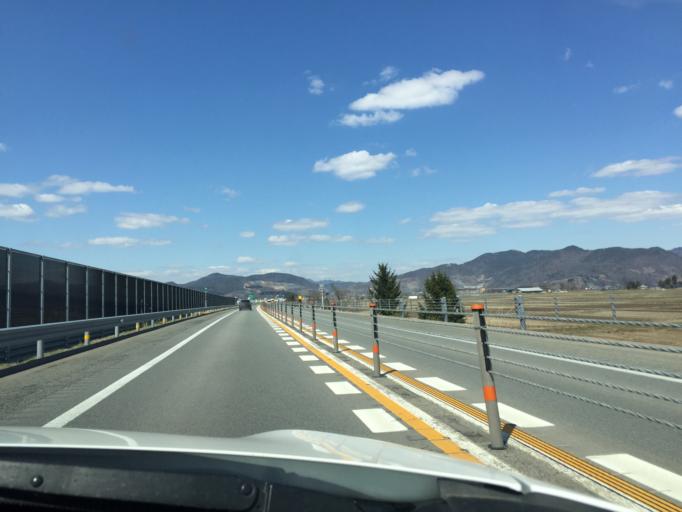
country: JP
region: Yamagata
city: Takahata
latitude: 38.0141
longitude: 140.1576
